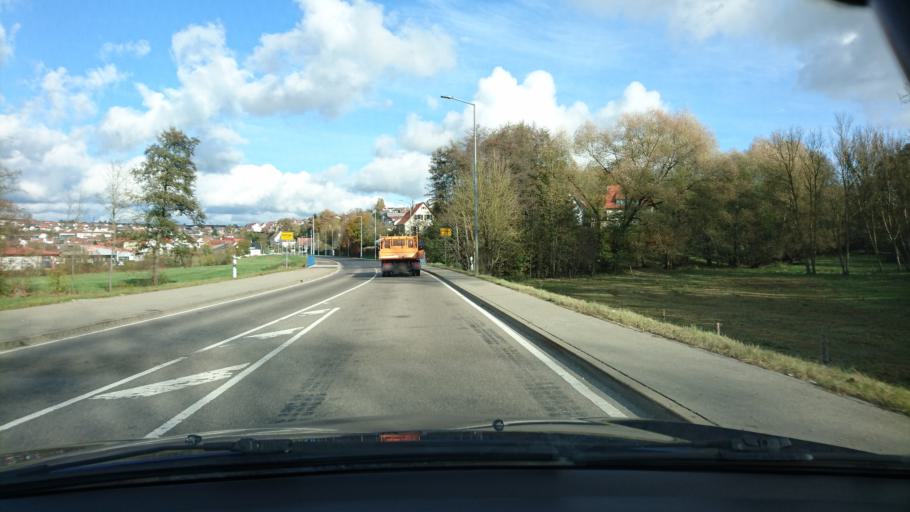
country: DE
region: Baden-Wuerttemberg
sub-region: Regierungsbezirk Stuttgart
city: Huttlingen
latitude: 48.8842
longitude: 10.0981
